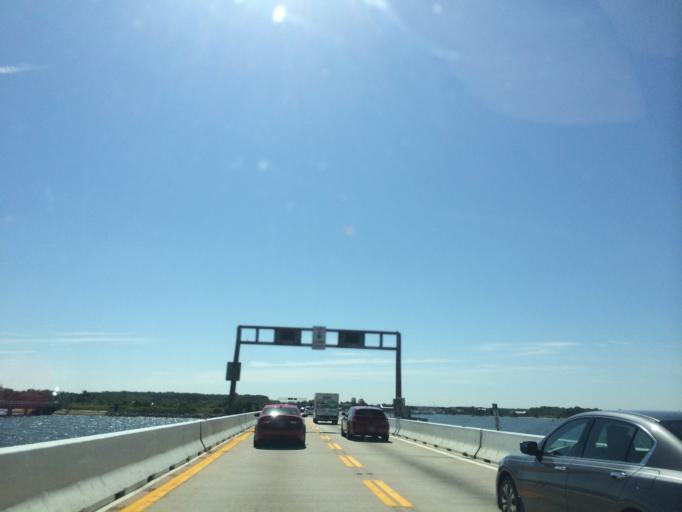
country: US
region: Maryland
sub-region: Queen Anne's County
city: Stevensville
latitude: 38.9844
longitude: -76.3445
